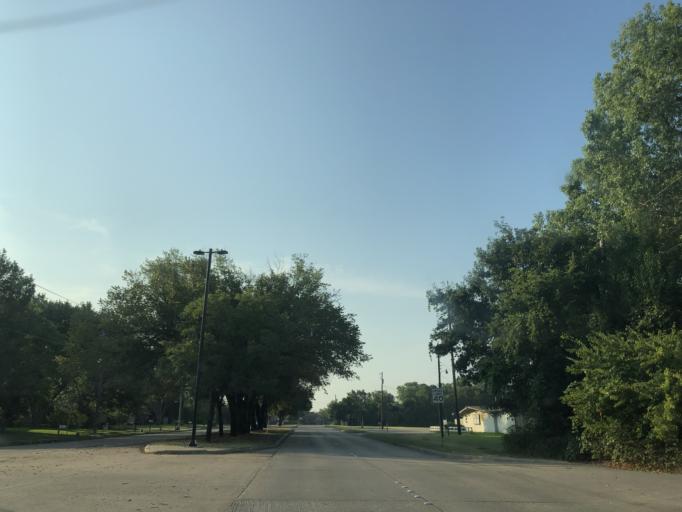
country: US
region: Texas
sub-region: Dallas County
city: Garland
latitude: 32.8706
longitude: -96.6300
